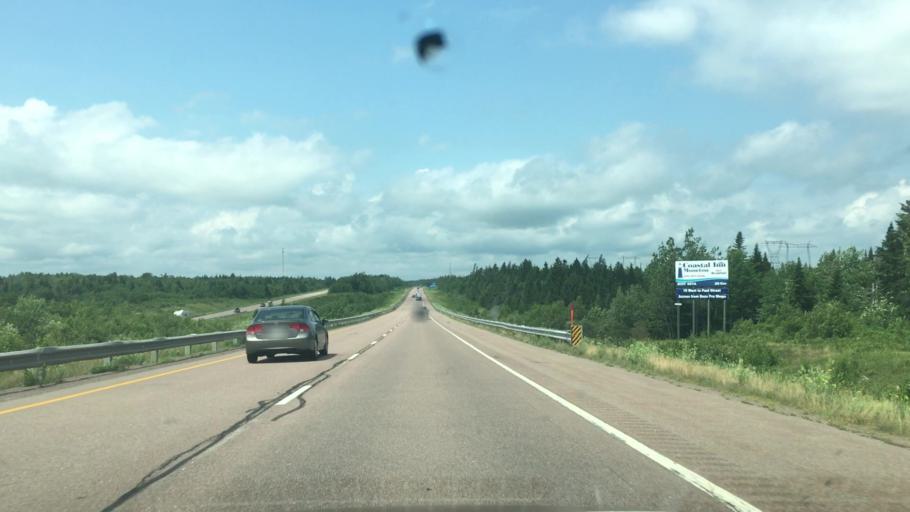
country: CA
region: New Brunswick
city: Sackville
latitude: 45.9855
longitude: -64.4734
